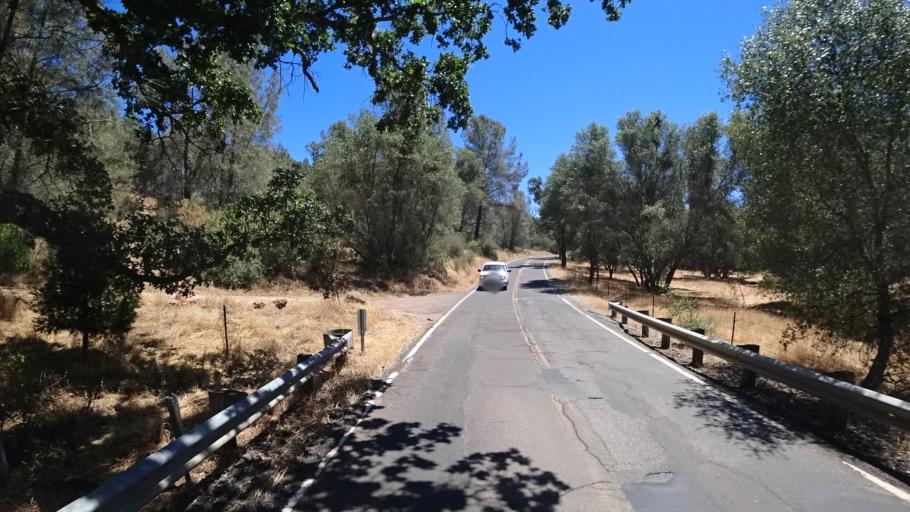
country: US
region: California
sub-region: Calaveras County
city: Copperopolis
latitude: 38.0593
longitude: -120.6526
